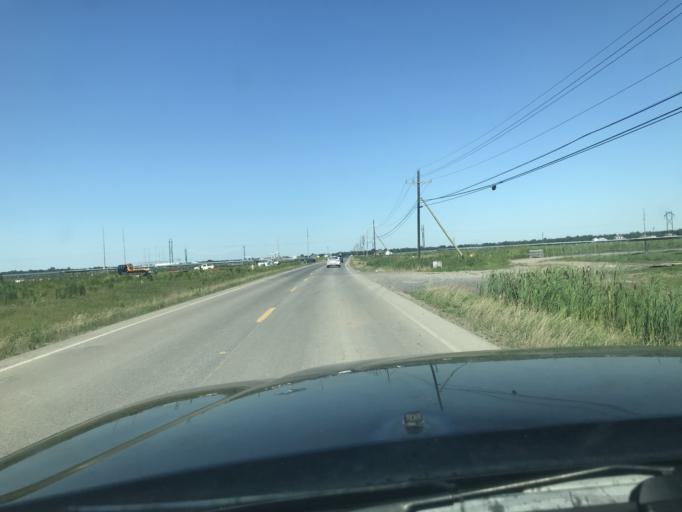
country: US
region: Louisiana
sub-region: West Baton Rouge Parish
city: Brusly
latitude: 30.4688
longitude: -91.3178
